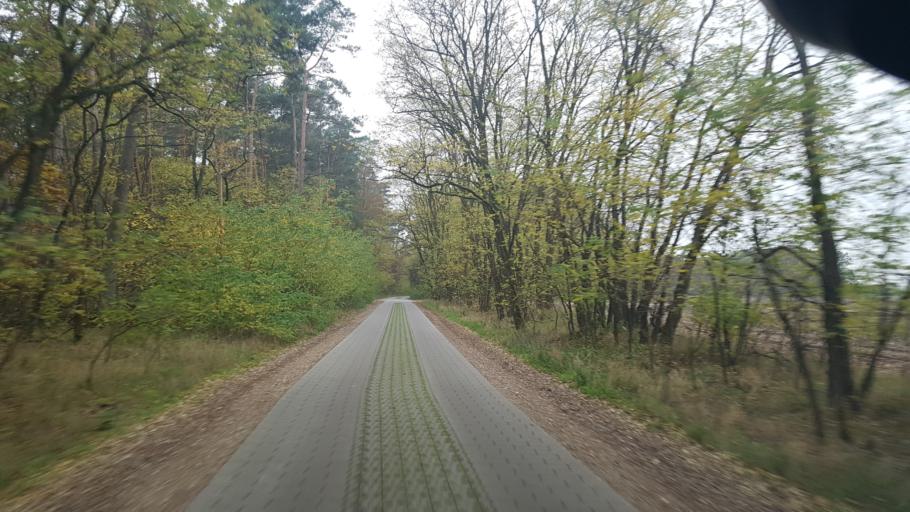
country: DE
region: Brandenburg
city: Lindow
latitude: 52.9398
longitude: 13.0332
